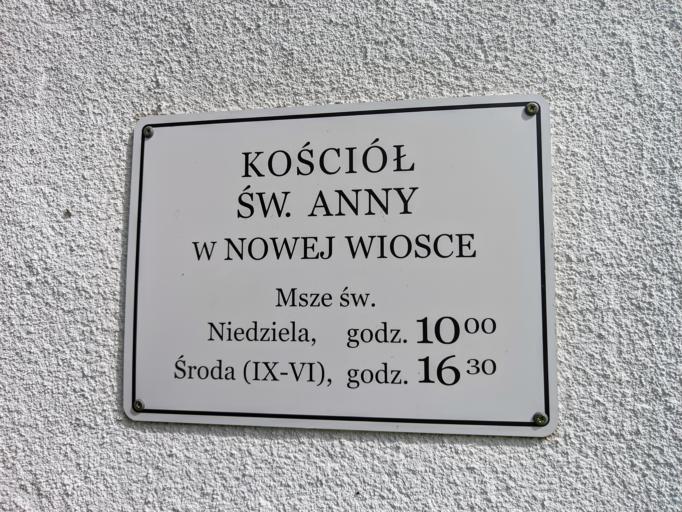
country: PL
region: Lubusz
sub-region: Powiat swiebodzinski
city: Lubrza
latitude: 52.2941
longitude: 15.4359
